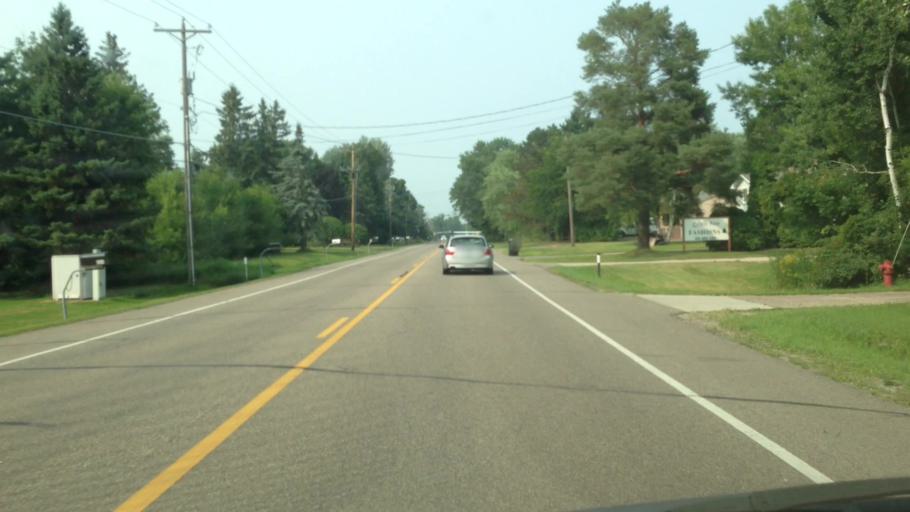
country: US
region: Minnesota
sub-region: Anoka County
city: Circle Pines
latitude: 45.1365
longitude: -93.1273
